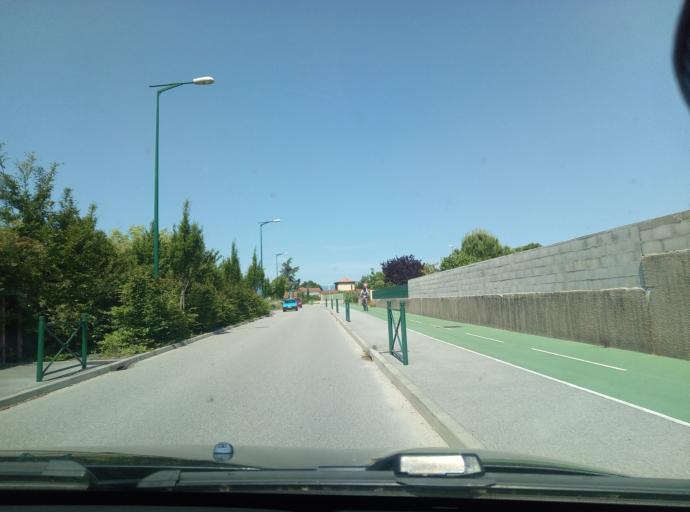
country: FR
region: Rhone-Alpes
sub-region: Departement de la Drome
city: Chanos-Curson
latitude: 45.0596
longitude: 4.9121
